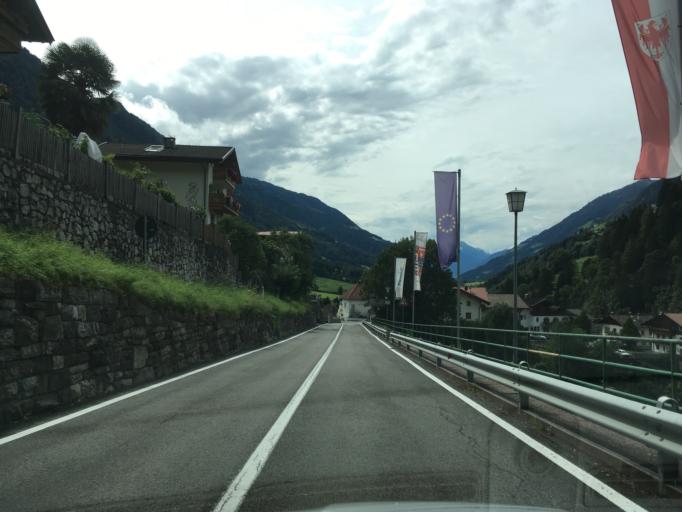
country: IT
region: Trentino-Alto Adige
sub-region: Bolzano
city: San Leonardo in Passiria
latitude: 46.8147
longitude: 11.2447
